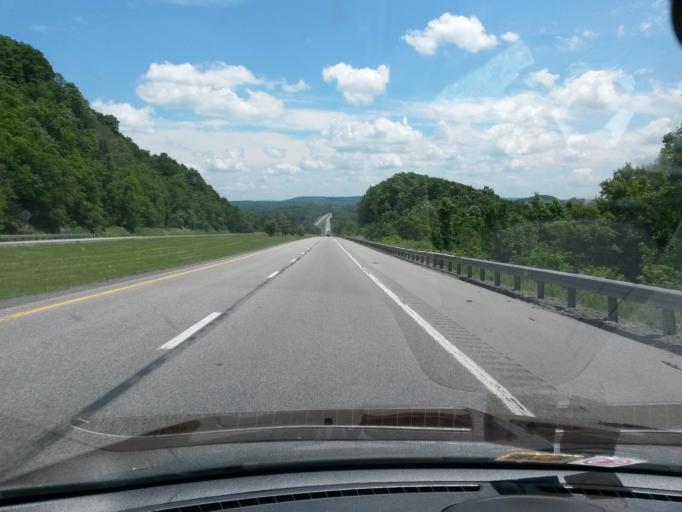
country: US
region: West Virginia
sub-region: Greenbrier County
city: Lewisburg
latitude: 37.8997
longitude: -80.5914
